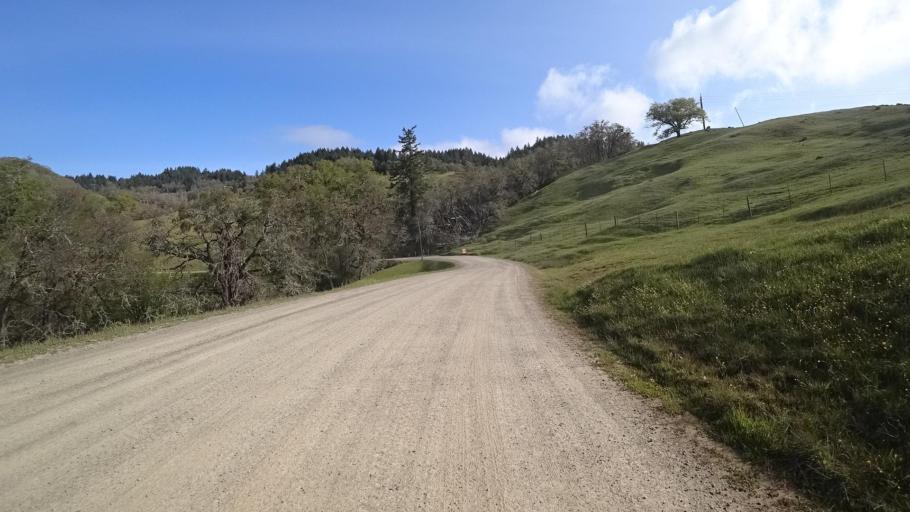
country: US
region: California
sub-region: Humboldt County
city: Hydesville
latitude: 40.6402
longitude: -123.8888
